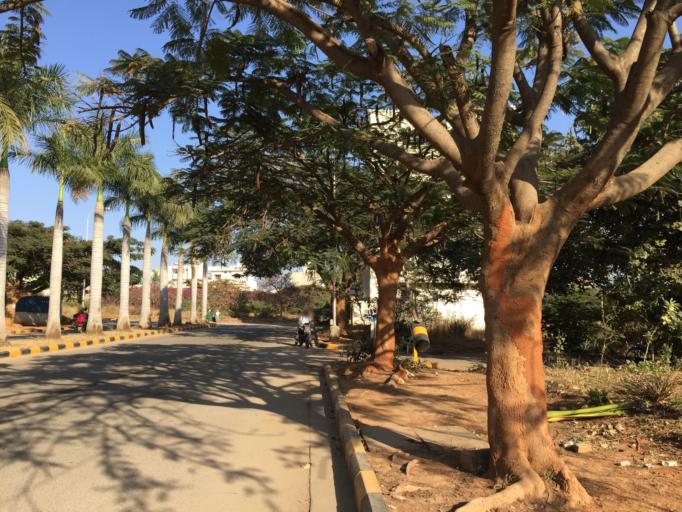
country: IN
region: Karnataka
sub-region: Bangalore Urban
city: Yelahanka
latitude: 13.0535
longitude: 77.6246
